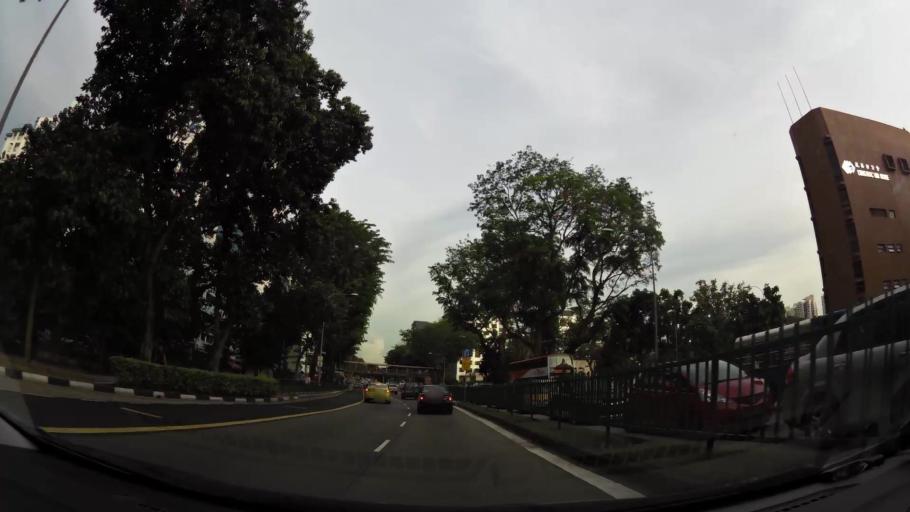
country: SG
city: Singapore
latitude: 1.2865
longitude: 103.8060
